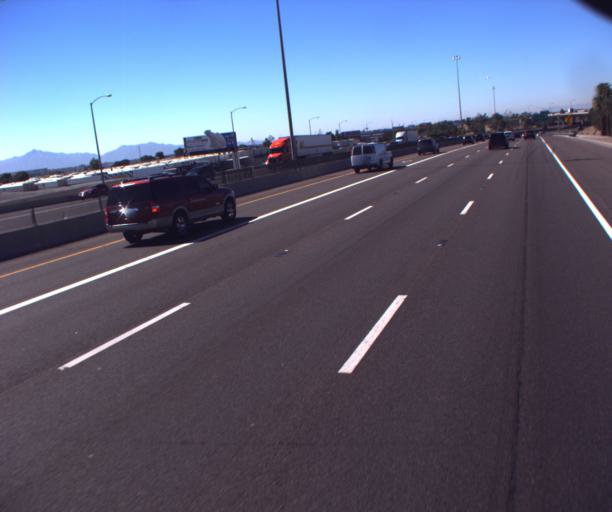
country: US
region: Arizona
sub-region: Maricopa County
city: Phoenix
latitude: 33.4270
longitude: -112.0316
